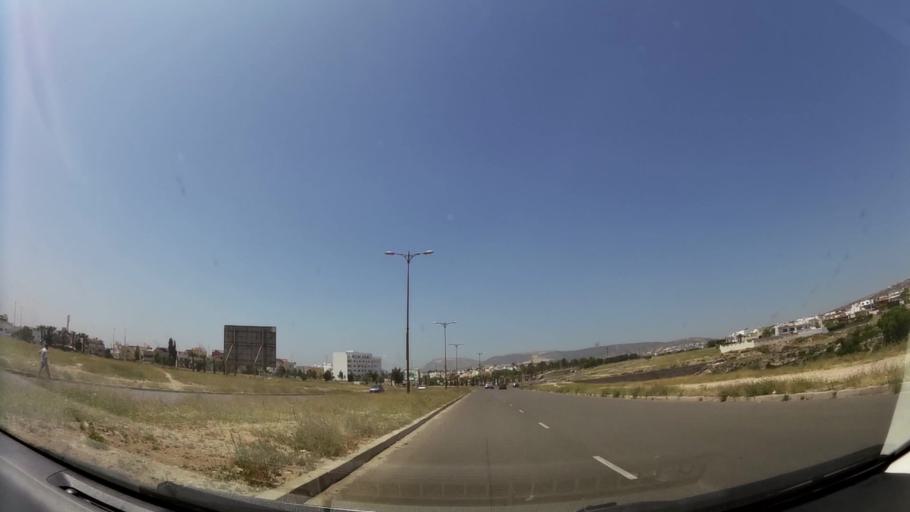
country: MA
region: Souss-Massa-Draa
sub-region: Agadir-Ida-ou-Tnan
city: Agadir
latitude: 30.4358
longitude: -9.5765
